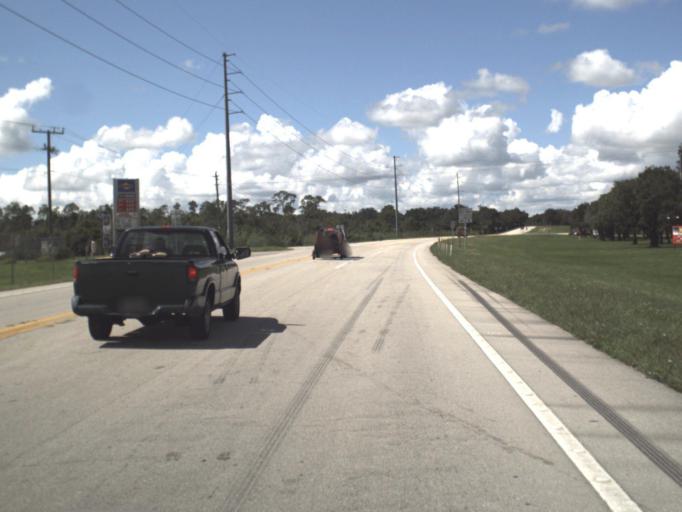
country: US
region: Florida
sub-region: DeSoto County
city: Arcadia
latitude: 27.2250
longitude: -81.8875
